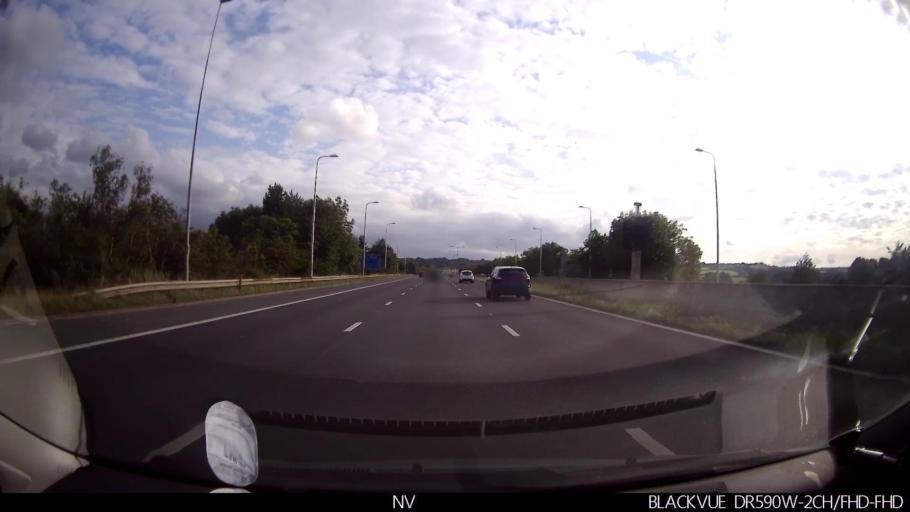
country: GB
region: England
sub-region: City and Borough of Leeds
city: Morley
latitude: 53.7687
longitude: -1.5910
